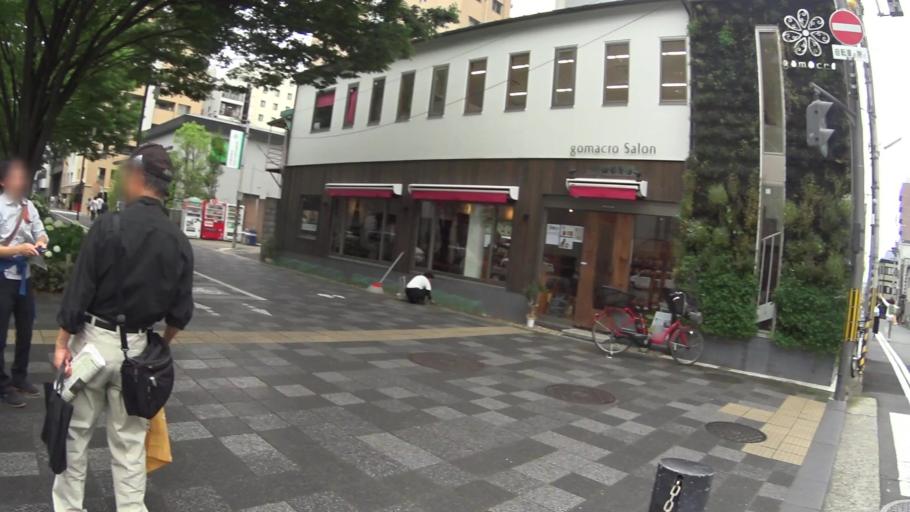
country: JP
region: Kyoto
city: Kyoto
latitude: 35.0107
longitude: 135.7565
